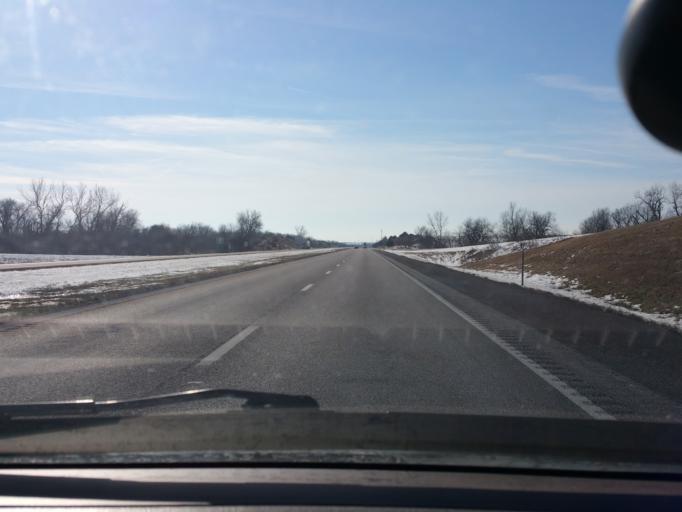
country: US
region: Missouri
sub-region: Clinton County
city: Cameron
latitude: 39.8996
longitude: -94.1516
